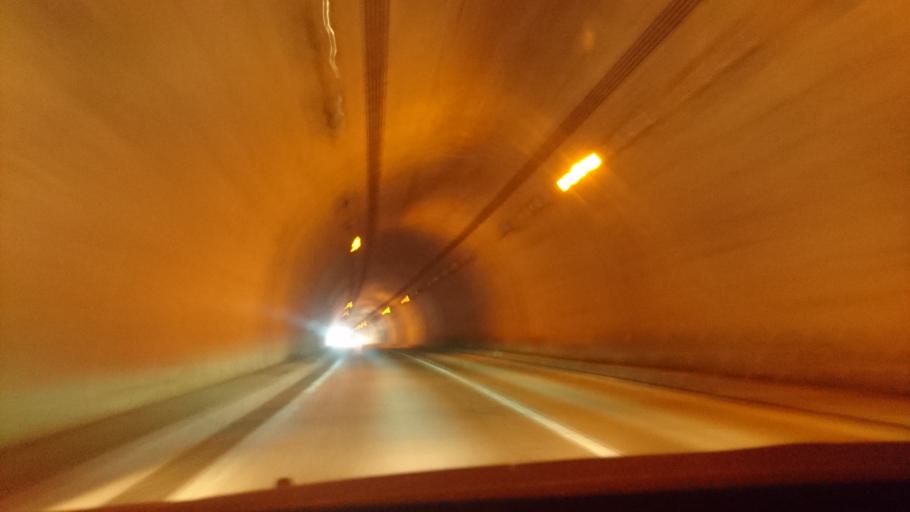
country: JP
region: Iwate
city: Mizusawa
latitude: 39.0316
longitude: 141.2645
